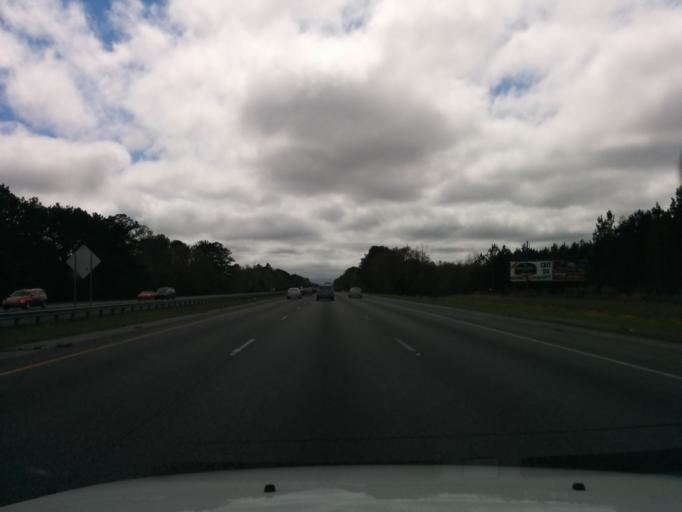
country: US
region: Georgia
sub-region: Chatham County
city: Pooler
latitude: 32.0565
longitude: -81.2551
